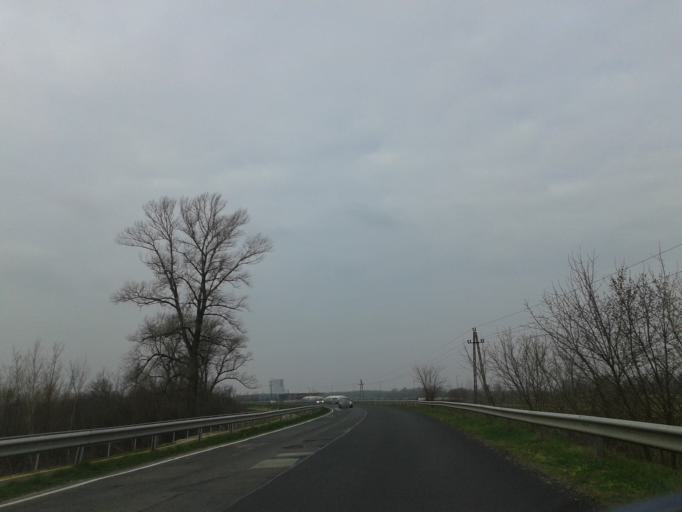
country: HU
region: Gyor-Moson-Sopron
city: Bony
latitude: 47.7330
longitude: 17.7995
